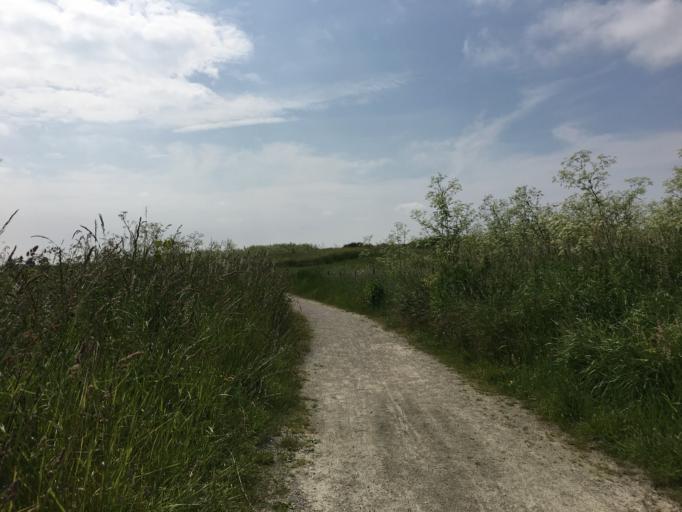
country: GB
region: England
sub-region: Kent
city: Sittingbourne
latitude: 51.3518
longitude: 0.7520
